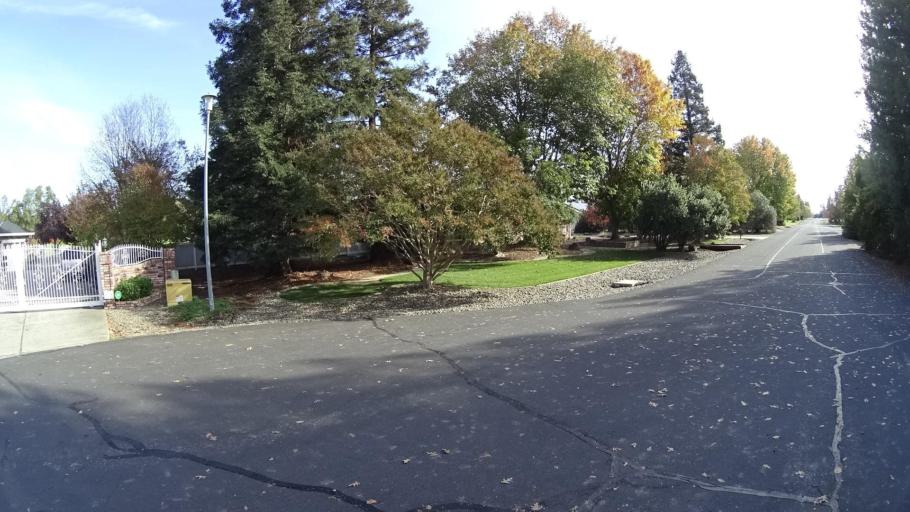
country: US
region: California
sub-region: Sacramento County
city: Vineyard
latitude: 38.4412
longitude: -121.3640
